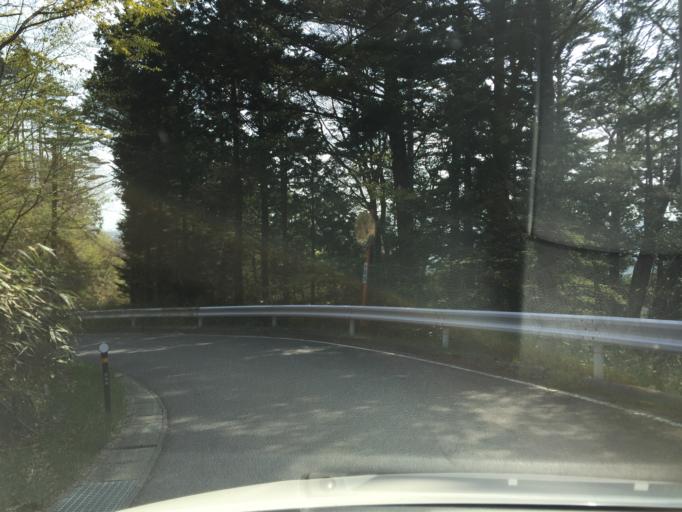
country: JP
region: Fukushima
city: Iwaki
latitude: 37.2000
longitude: 140.8508
